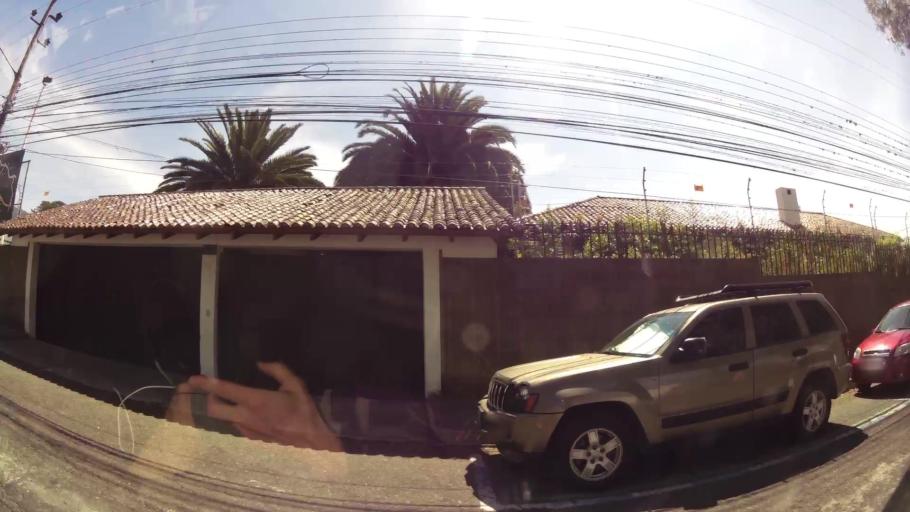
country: EC
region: Pichincha
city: Quito
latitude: -0.1944
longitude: -78.4380
